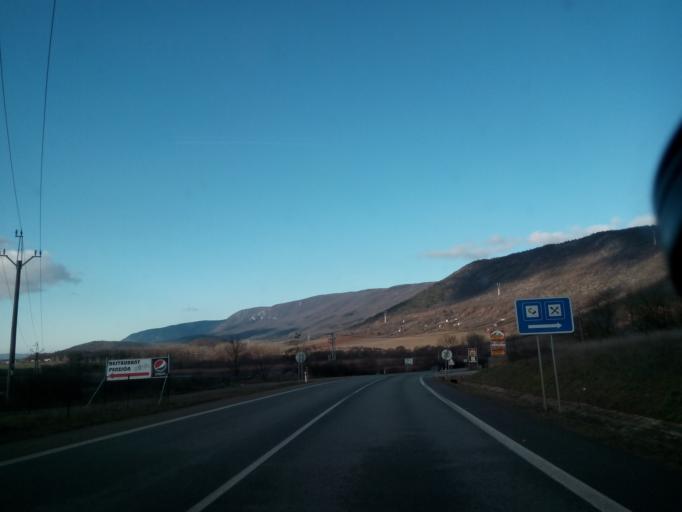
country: SK
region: Kosicky
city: Medzev
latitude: 48.6054
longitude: 20.8729
